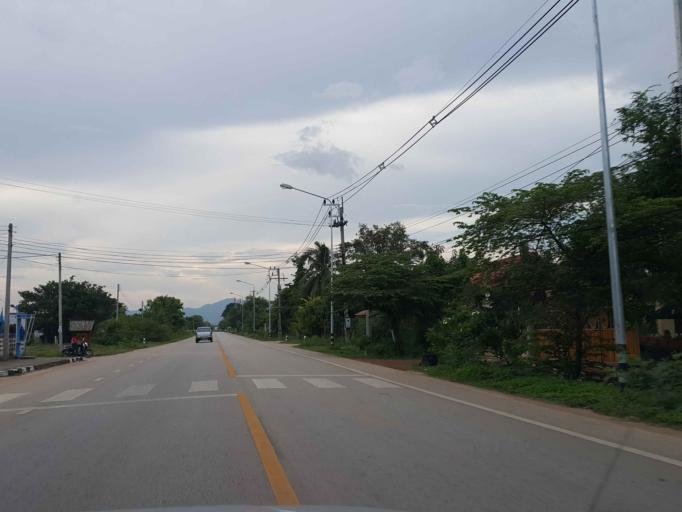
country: TH
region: Lampang
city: Hang Chat
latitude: 18.2866
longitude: 99.3788
